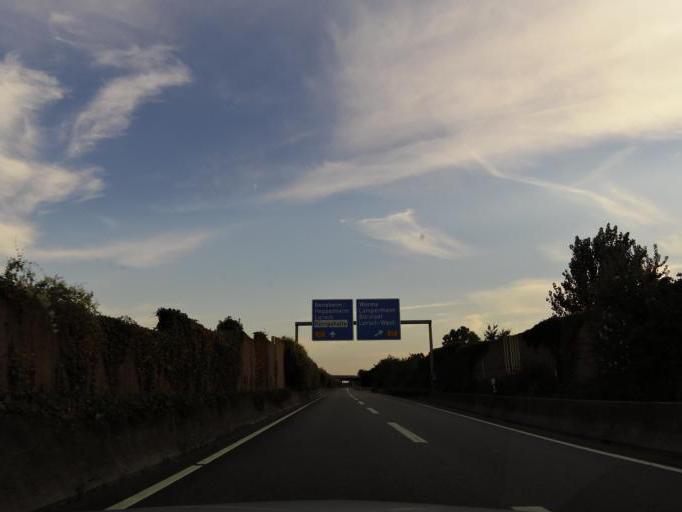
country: DE
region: Hesse
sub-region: Regierungsbezirk Darmstadt
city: Einhausen
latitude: 49.6635
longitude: 8.5546
